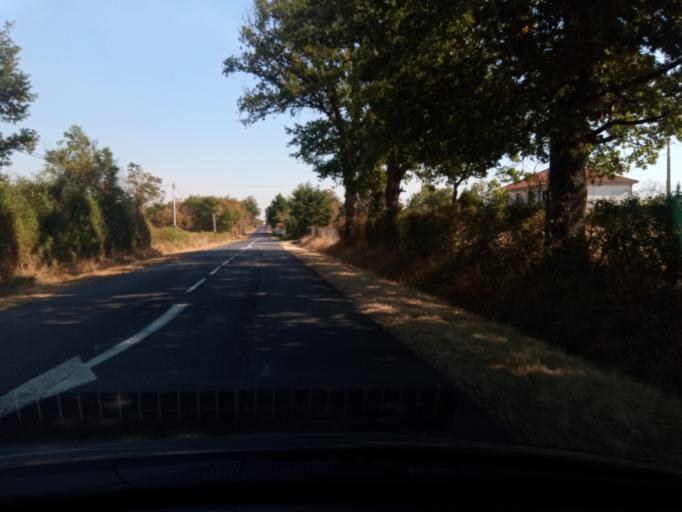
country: FR
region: Poitou-Charentes
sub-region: Departement de la Vienne
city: Montmorillon
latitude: 46.4308
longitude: 0.8501
